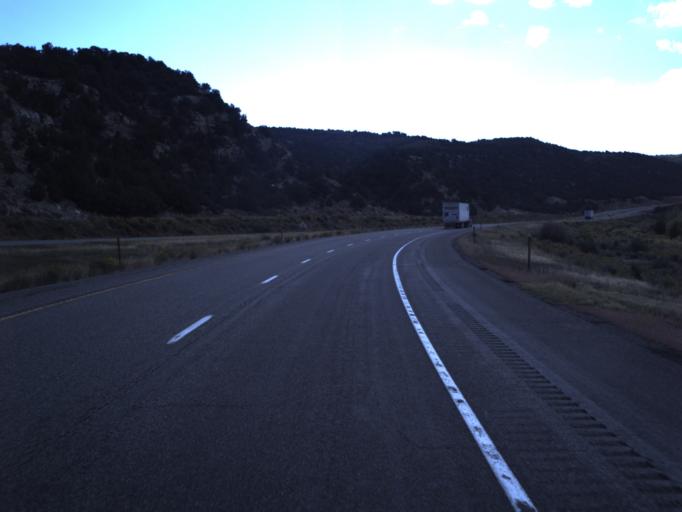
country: US
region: Utah
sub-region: Sevier County
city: Salina
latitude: 38.8491
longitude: -111.5414
